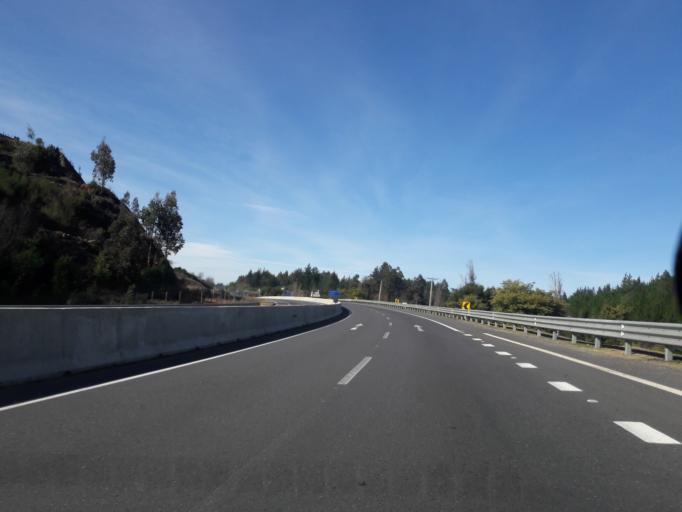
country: CL
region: Biobio
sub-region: Provincia de Biobio
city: Yumbel
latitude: -36.9577
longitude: -72.7430
